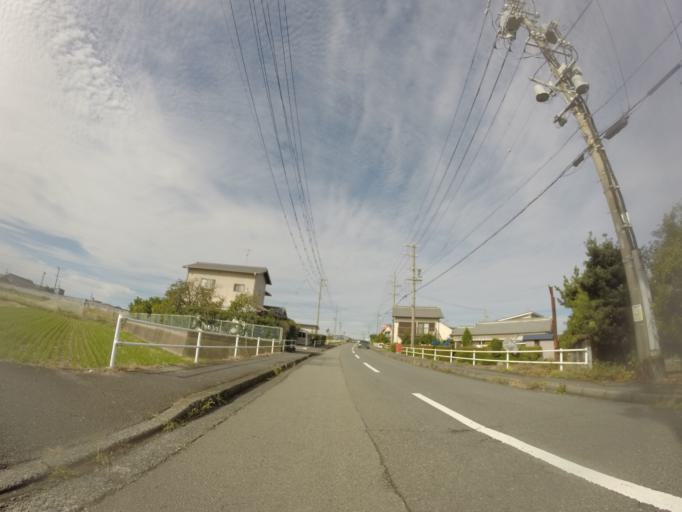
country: JP
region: Shizuoka
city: Shimada
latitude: 34.7684
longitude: 138.2594
